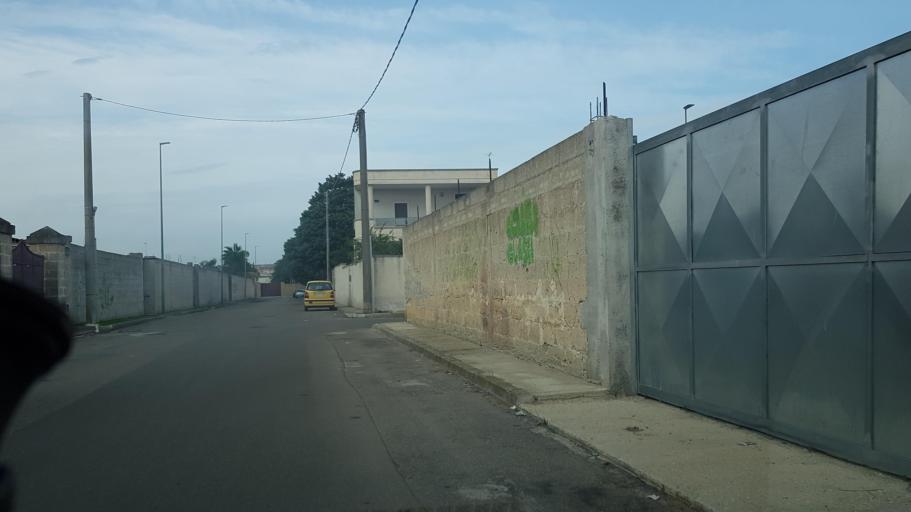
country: IT
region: Apulia
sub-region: Provincia di Lecce
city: Trepuzzi
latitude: 40.4037
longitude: 18.0668
